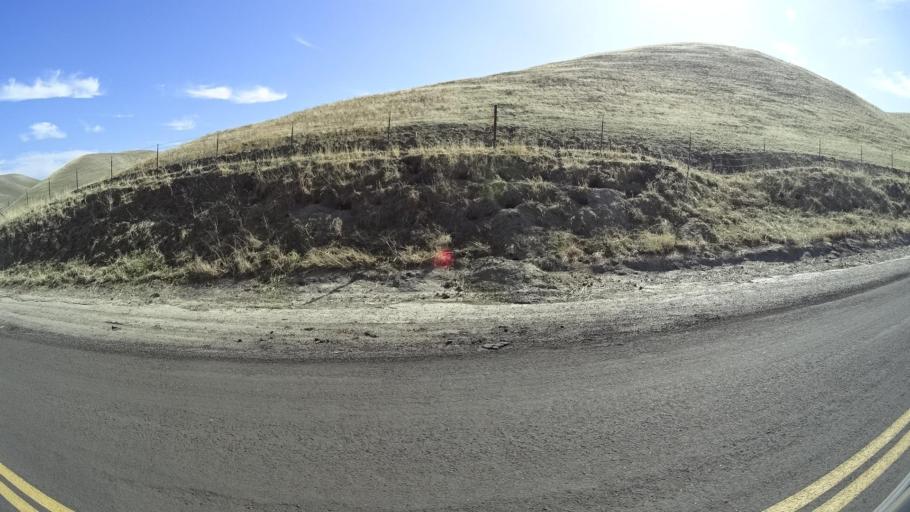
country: US
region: California
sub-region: Tulare County
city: Richgrove
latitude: 35.6643
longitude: -118.9162
